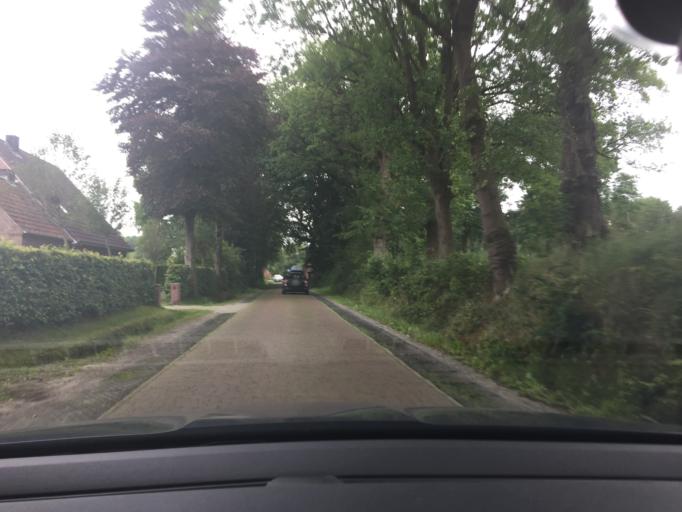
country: DE
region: Lower Saxony
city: Aurich
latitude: 53.4478
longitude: 7.4808
